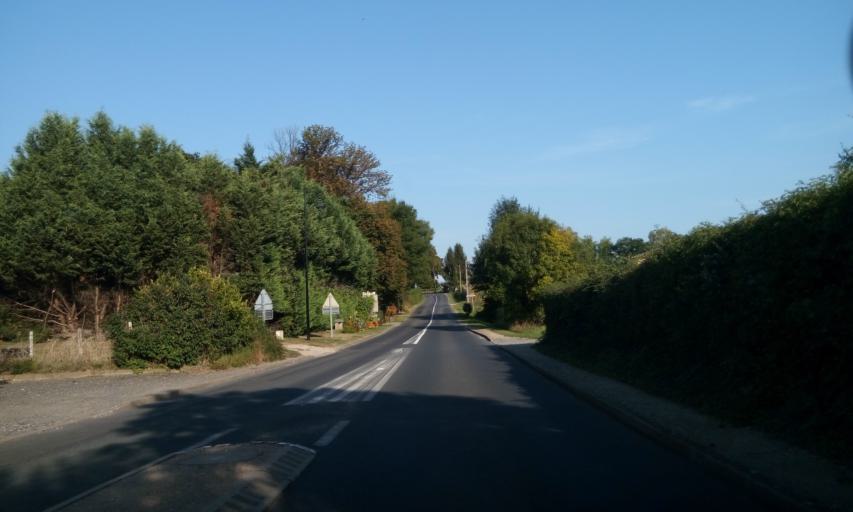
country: FR
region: Rhone-Alpes
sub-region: Departement de l'Ain
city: Villeneuve
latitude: 46.0007
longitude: 4.8510
